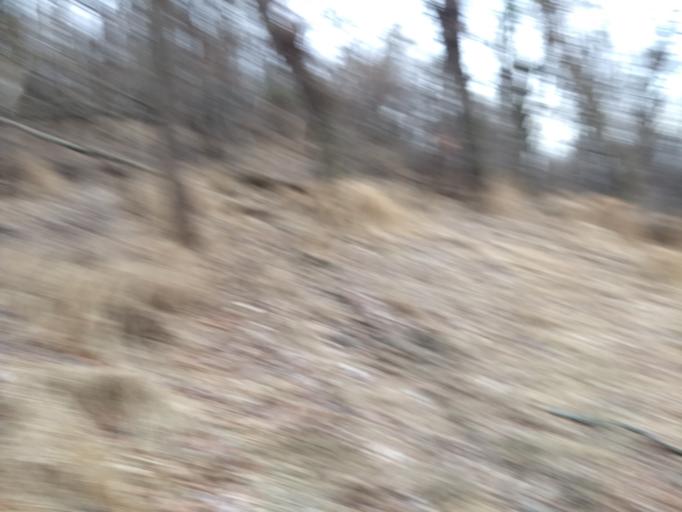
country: US
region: Pennsylvania
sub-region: Allegheny County
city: Homestead
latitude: 40.4097
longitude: -79.9368
